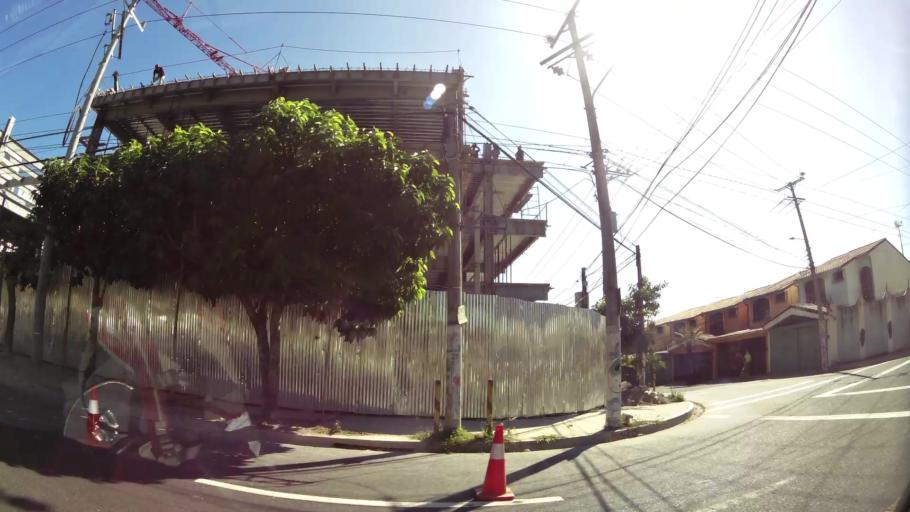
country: SV
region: La Libertad
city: Santa Tecla
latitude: 13.6773
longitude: -89.2771
